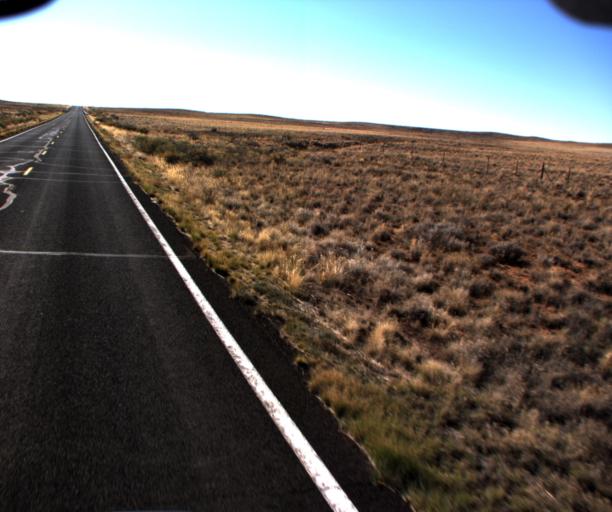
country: US
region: Arizona
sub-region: Navajo County
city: First Mesa
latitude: 35.6491
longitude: -110.4888
